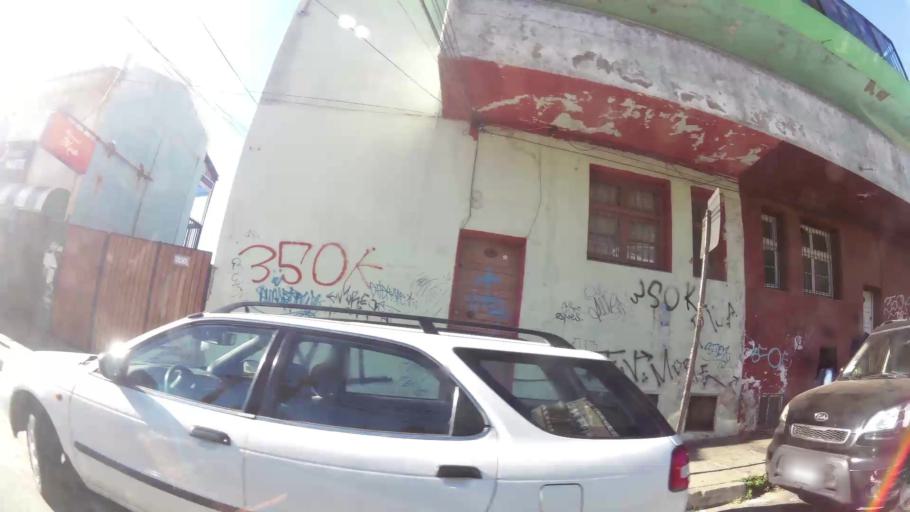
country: CL
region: Valparaiso
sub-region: Provincia de Valparaiso
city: Valparaiso
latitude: -33.0543
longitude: -71.6240
